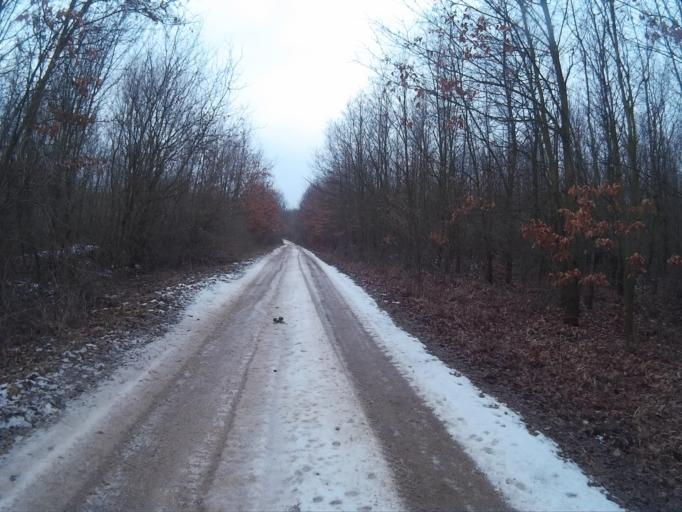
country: HU
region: Komarom-Esztergom
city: Tarjan
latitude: 47.5808
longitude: 18.5269
